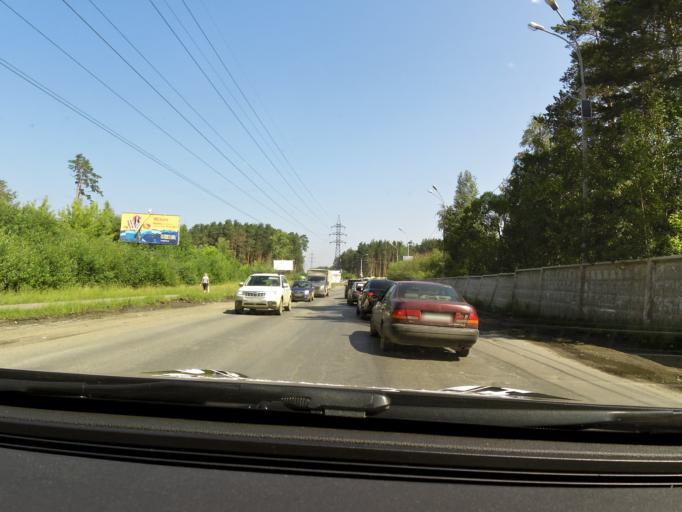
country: RU
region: Sverdlovsk
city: Shirokaya Rechka
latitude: 56.8151
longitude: 60.5206
